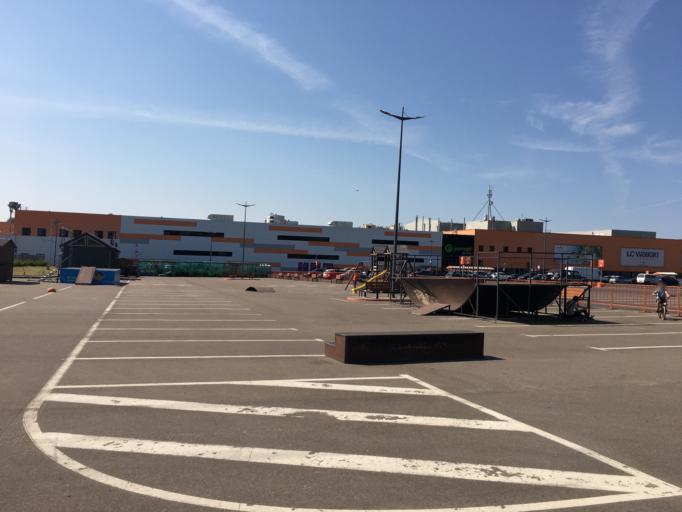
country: BY
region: Grodnenskaya
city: Hrodna
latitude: 53.7032
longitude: 23.8359
